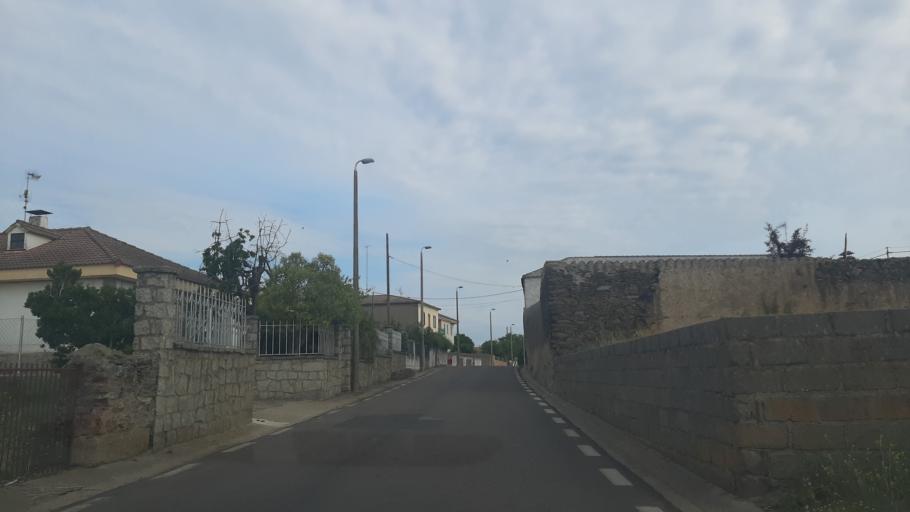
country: ES
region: Castille and Leon
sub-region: Provincia de Salamanca
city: Gallegos de Arganan
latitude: 40.6304
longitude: -6.7045
